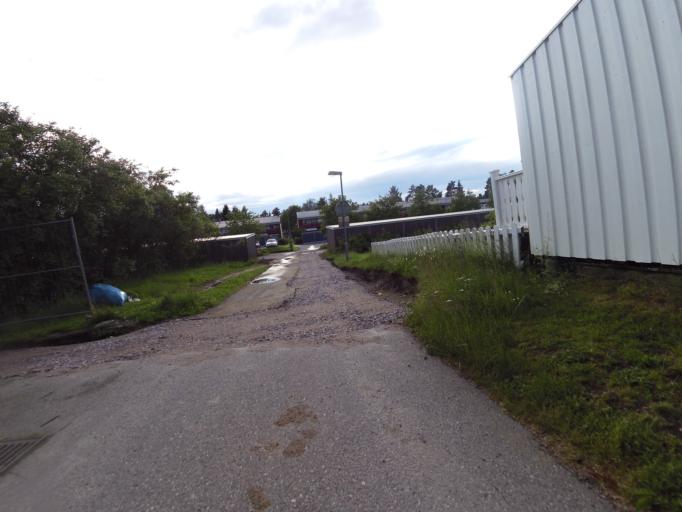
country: SE
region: Gaevleborg
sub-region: Gavle Kommun
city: Gavle
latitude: 60.6941
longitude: 17.1023
